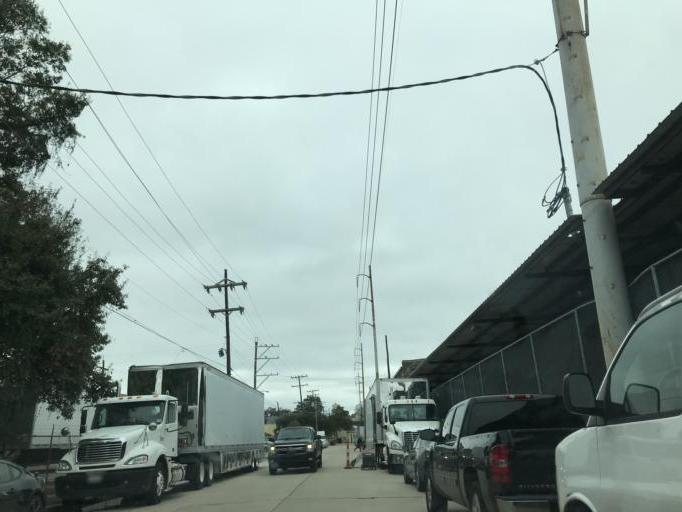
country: US
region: Louisiana
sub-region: Jefferson Parish
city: Gretna
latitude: 29.9305
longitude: -90.0692
